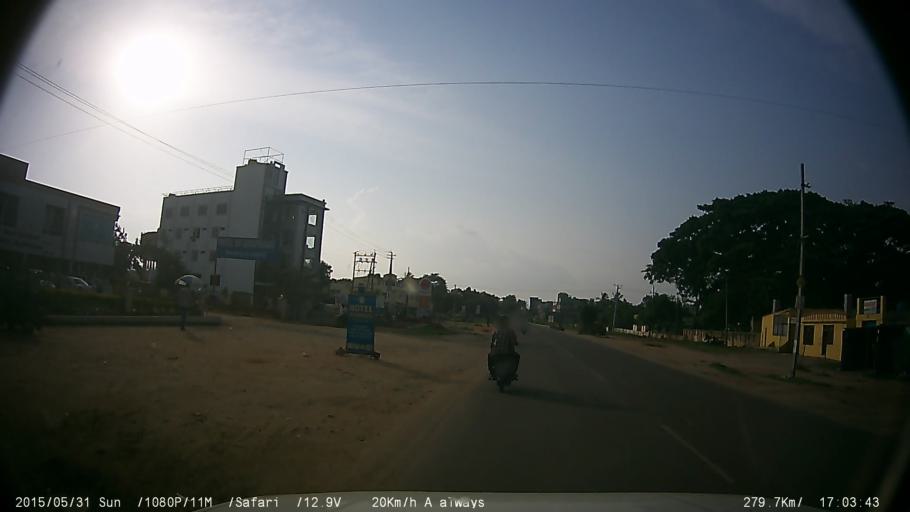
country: IN
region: Karnataka
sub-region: Chamrajnagar
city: Gundlupet
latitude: 11.8143
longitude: 76.6860
